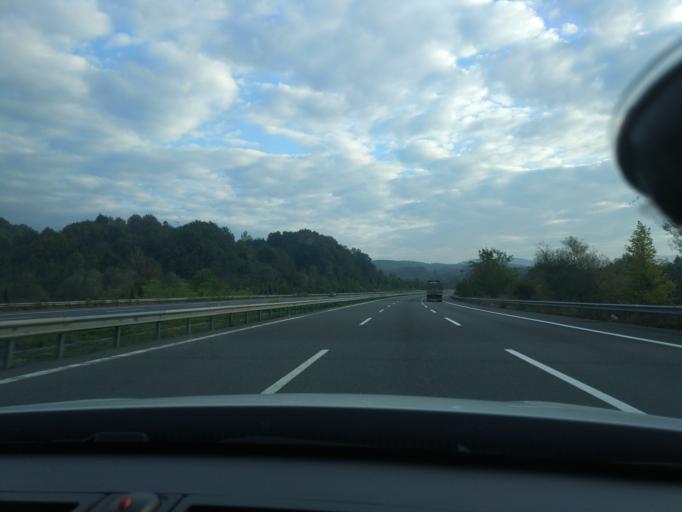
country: TR
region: Sakarya
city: Hendek
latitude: 40.7747
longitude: 30.7850
